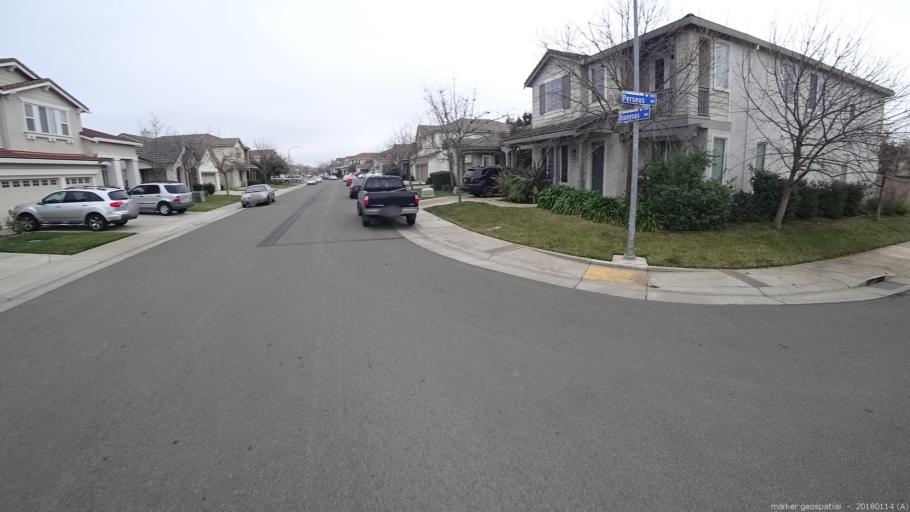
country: US
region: California
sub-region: Sacramento County
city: Rancho Cordova
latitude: 38.5510
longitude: -121.2408
